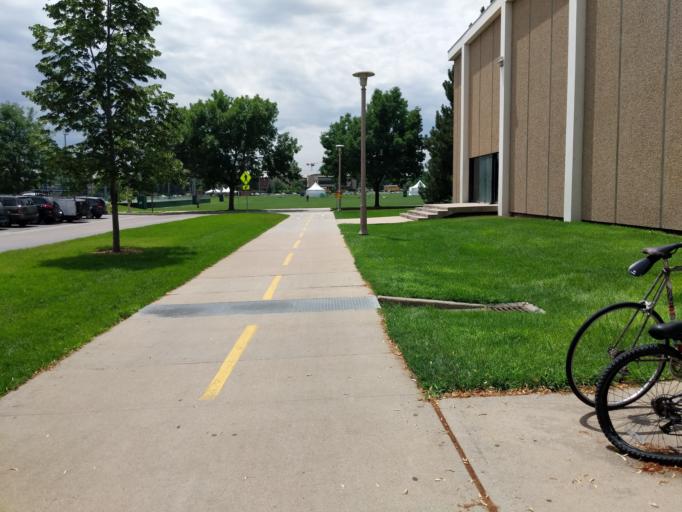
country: US
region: Colorado
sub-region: Larimer County
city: Fort Collins
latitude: 40.5756
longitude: -105.0912
